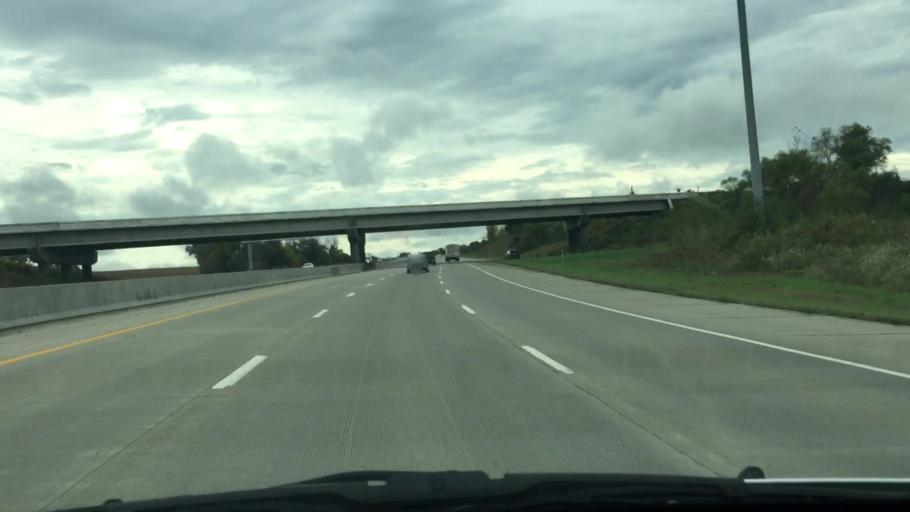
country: US
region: Iowa
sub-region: Polk County
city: West Des Moines
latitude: 41.5205
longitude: -93.7743
